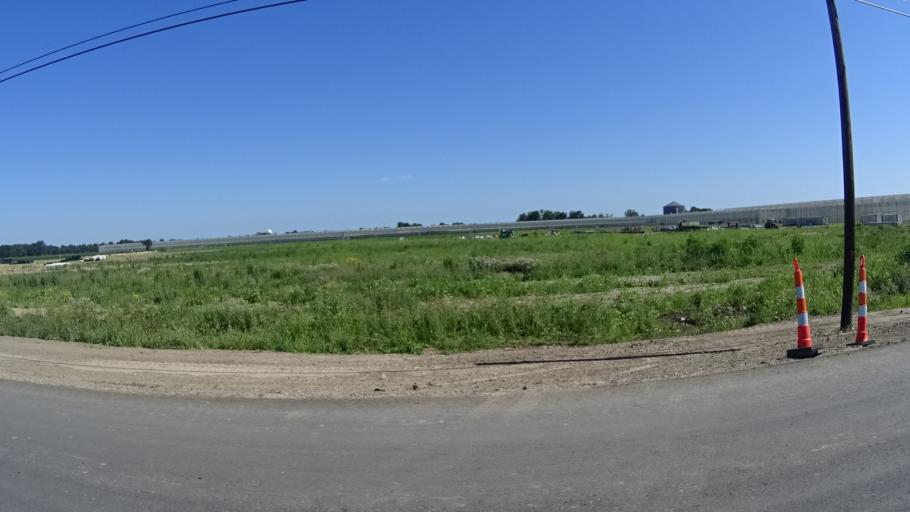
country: US
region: Ohio
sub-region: Erie County
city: Huron
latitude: 41.3892
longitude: -82.5941
